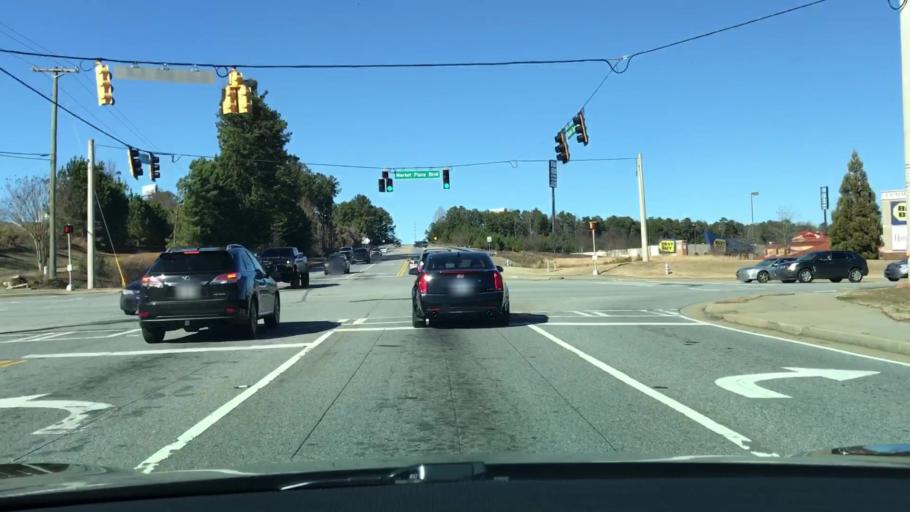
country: US
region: Georgia
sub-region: Forsyth County
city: Cumming
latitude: 34.1899
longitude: -84.1298
